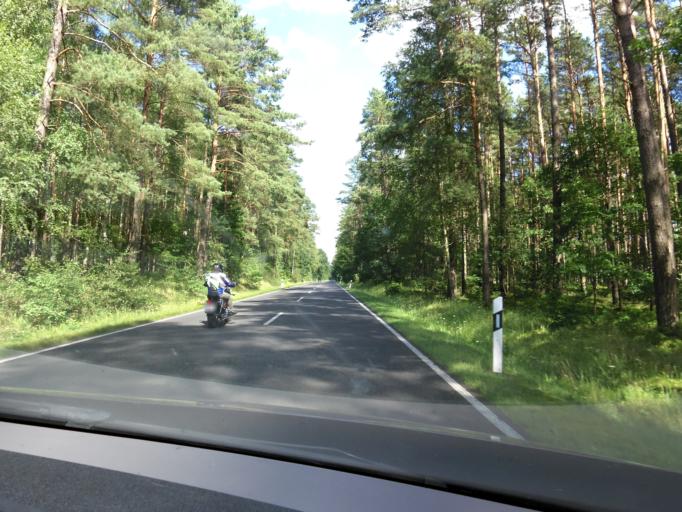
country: DE
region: Brandenburg
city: Furstenberg
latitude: 53.2009
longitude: 13.2115
